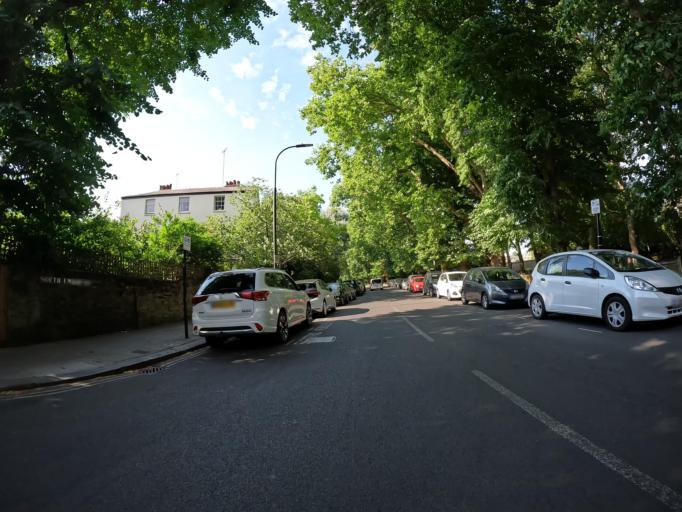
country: GB
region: England
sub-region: Greater London
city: Barnet
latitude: 51.6487
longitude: -0.1887
